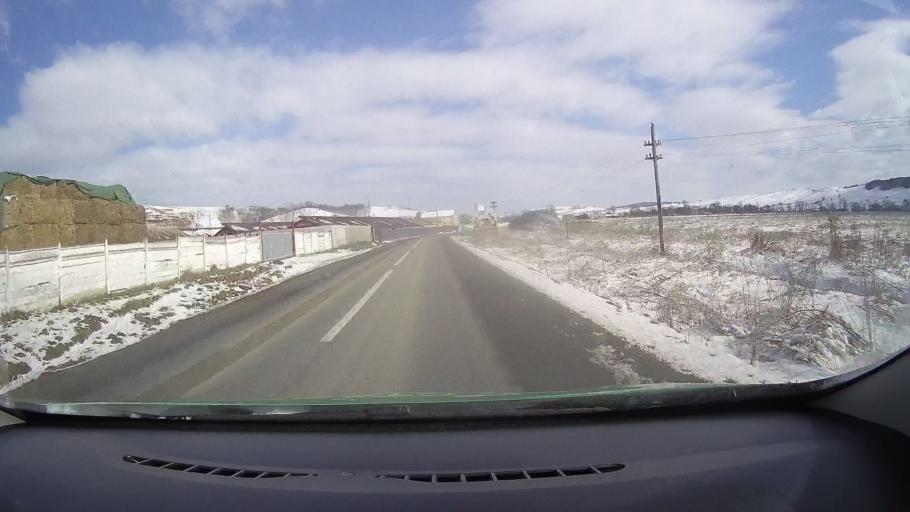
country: RO
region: Sibiu
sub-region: Oras Agnita
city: Agnita
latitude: 45.9645
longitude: 24.5789
